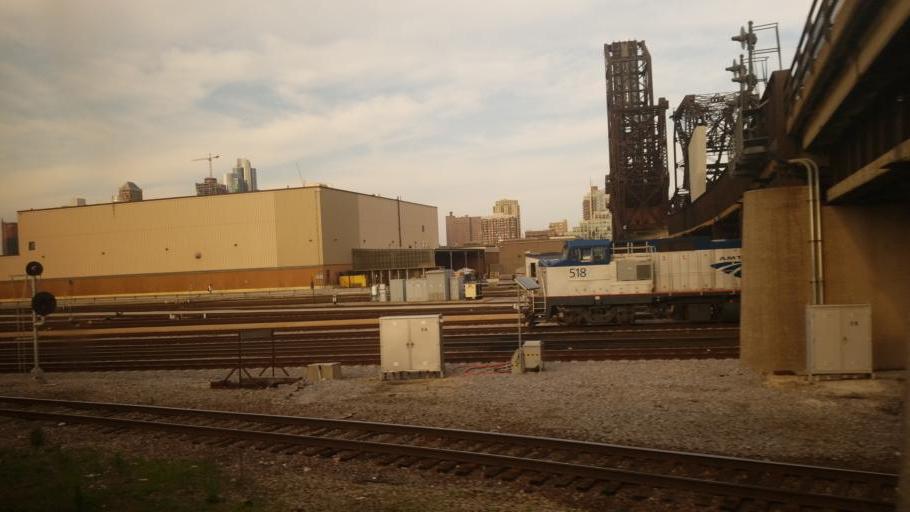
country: US
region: Illinois
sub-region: Cook County
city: Chicago
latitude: 41.8608
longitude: -87.6373
